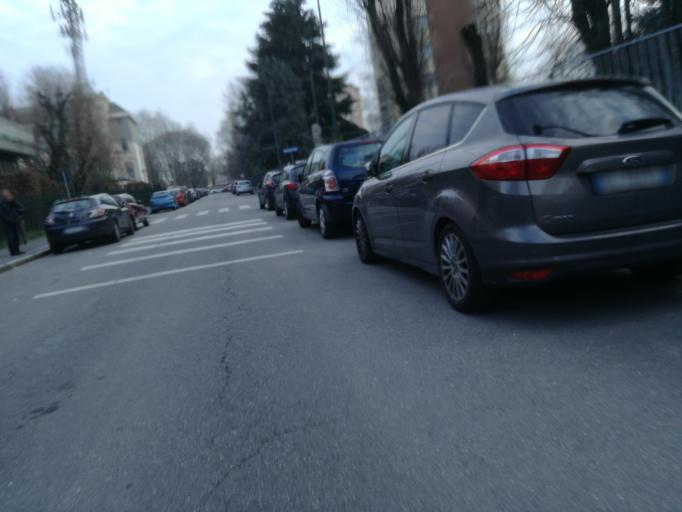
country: IT
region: Lombardy
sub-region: Citta metropolitana di Milano
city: Romano Banco
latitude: 45.4537
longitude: 9.1280
